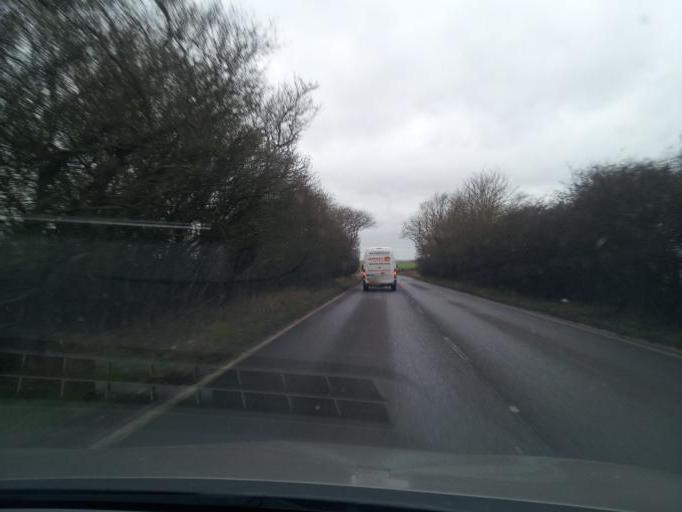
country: GB
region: England
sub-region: Suffolk
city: Ixworth
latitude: 52.3286
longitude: 0.9115
